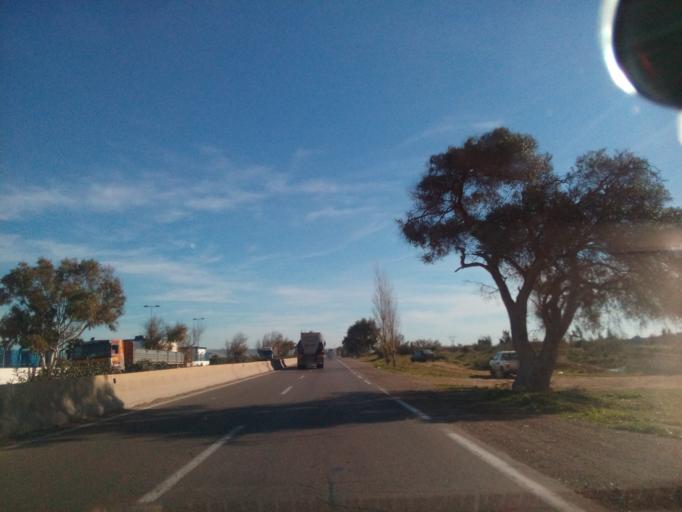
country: DZ
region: Oran
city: Ain el Bya
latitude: 35.7841
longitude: -0.1467
